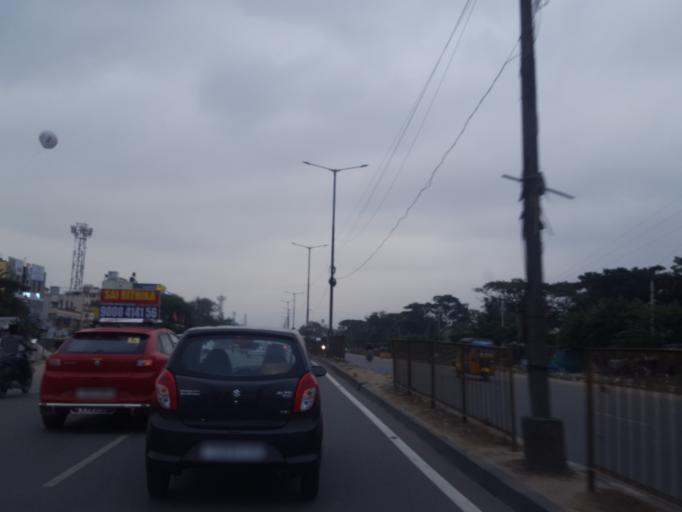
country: IN
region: Telangana
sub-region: Medak
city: Serilingampalle
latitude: 17.5069
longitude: 78.3042
